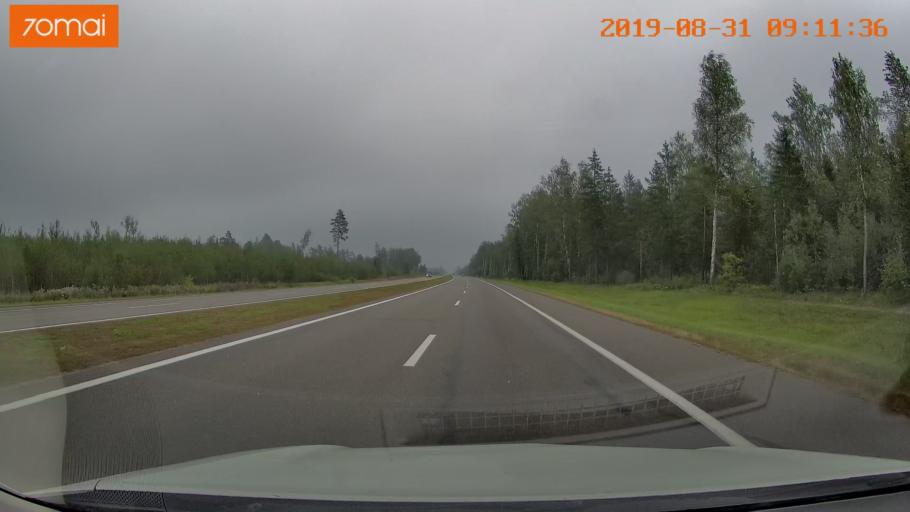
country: BY
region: Minsk
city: Chervyen'
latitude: 53.7423
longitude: 28.5645
